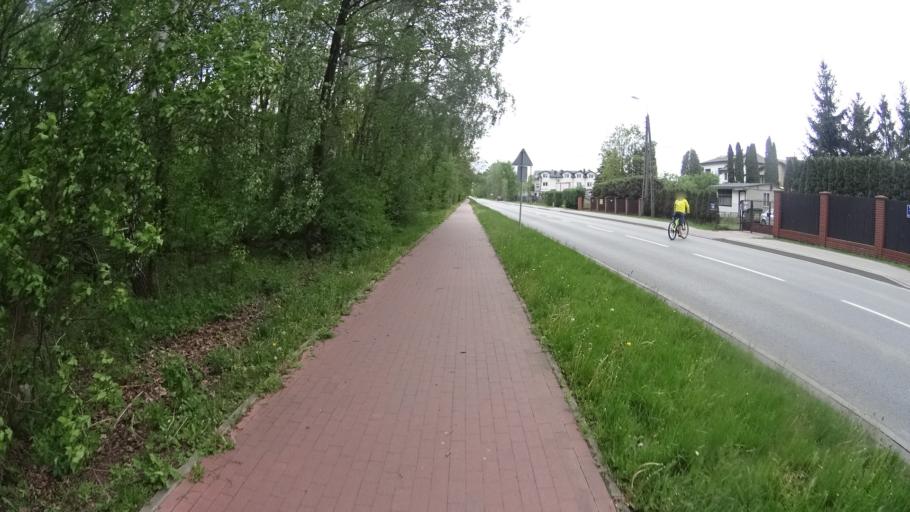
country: PL
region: Masovian Voivodeship
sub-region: Powiat warszawski zachodni
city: Babice
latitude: 52.2738
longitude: 20.8646
